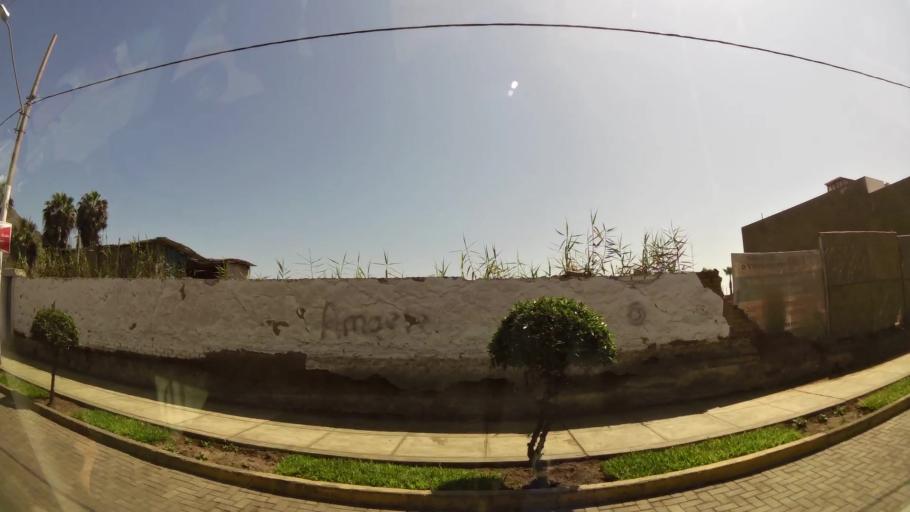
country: PE
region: Lima
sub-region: Provincia de Canete
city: San Vicente de Canete
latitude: -13.0280
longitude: -76.4815
